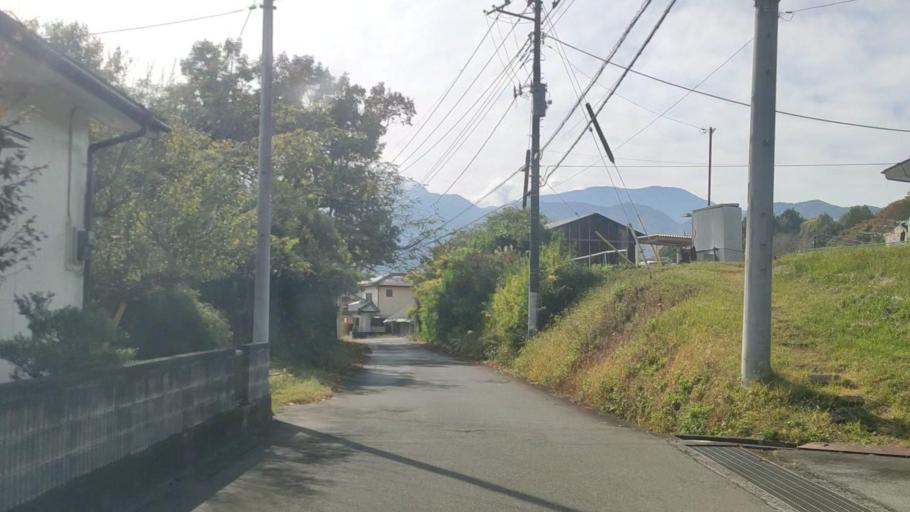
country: JP
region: Yamanashi
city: Ryuo
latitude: 35.4414
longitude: 138.4452
